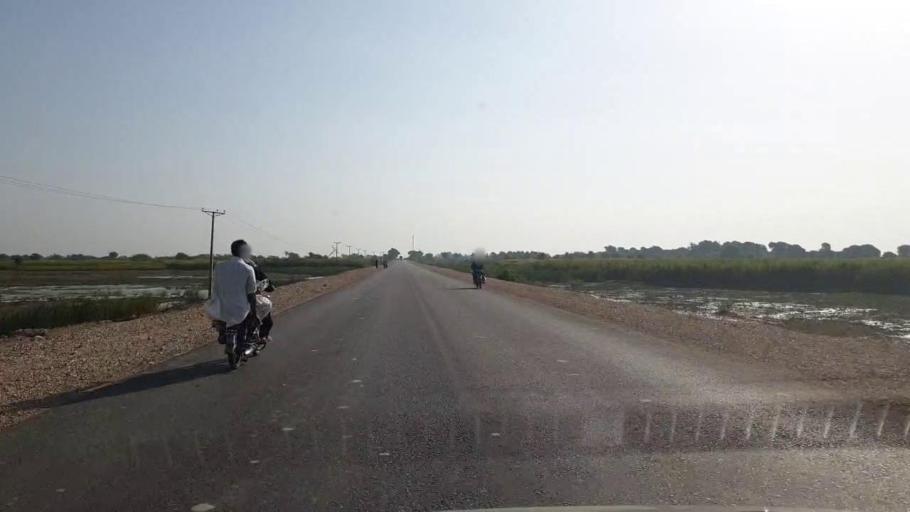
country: PK
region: Sindh
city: Badin
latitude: 24.6588
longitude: 68.9371
